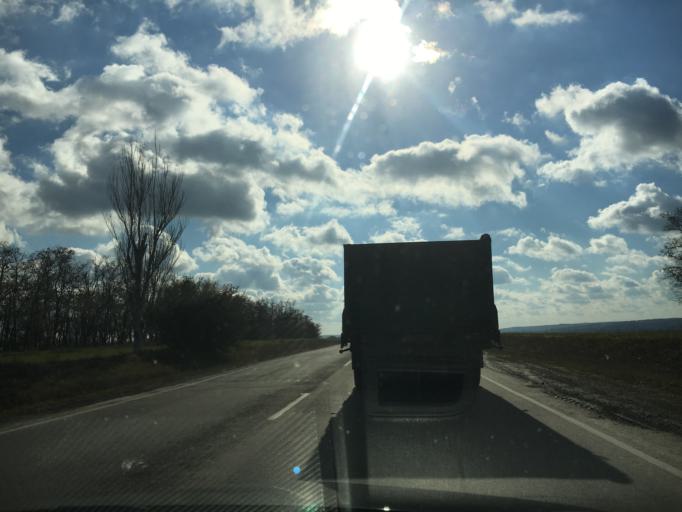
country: RU
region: Rostov
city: Matveyev Kurgan
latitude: 47.5409
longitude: 38.8914
